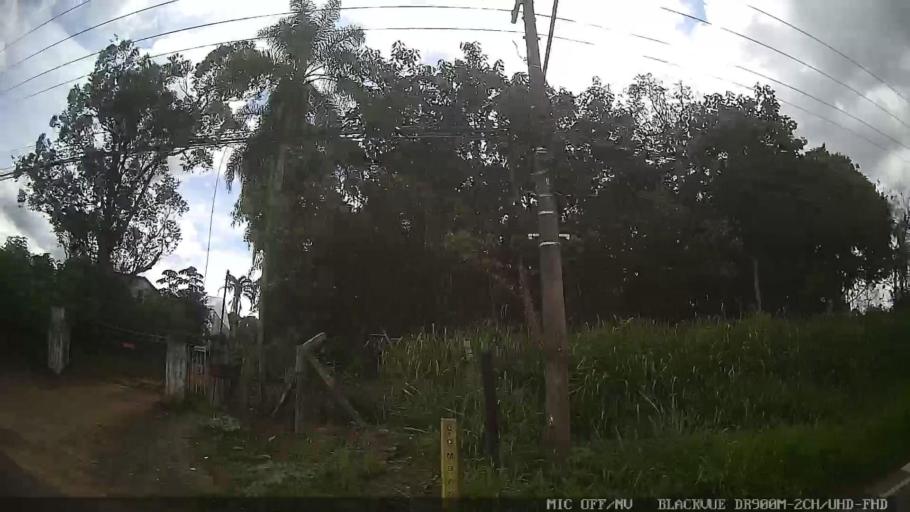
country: BR
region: Sao Paulo
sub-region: Suzano
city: Suzano
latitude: -23.5800
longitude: -46.3059
